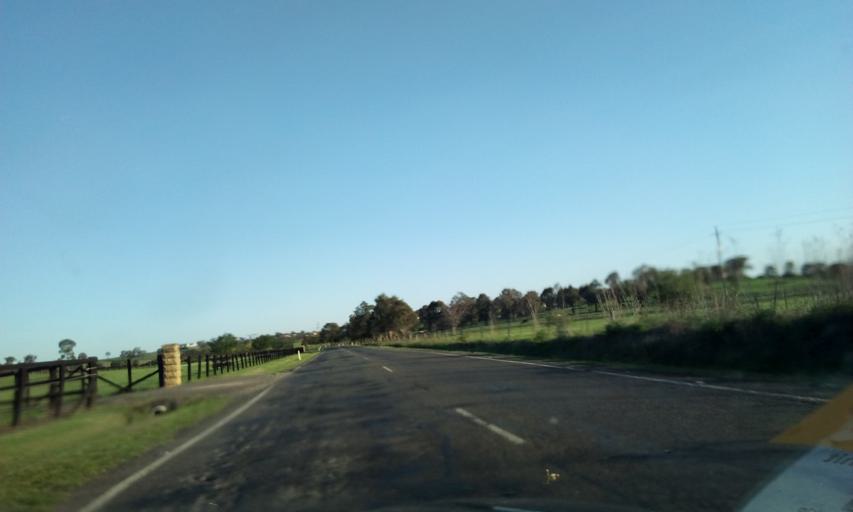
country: AU
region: New South Wales
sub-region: Wollondilly
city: Douglas Park
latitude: -34.1361
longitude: 150.7121
